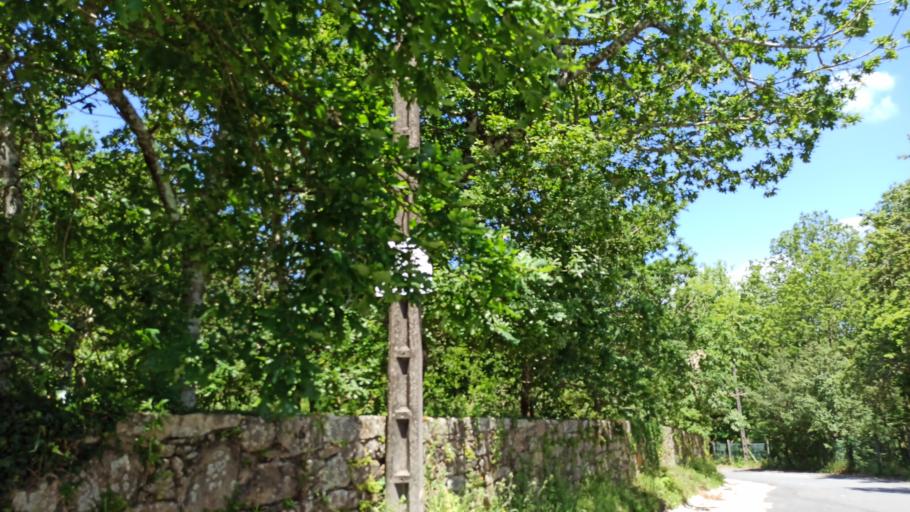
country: ES
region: Galicia
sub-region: Provincia da Coruna
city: Negreira
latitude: 42.9066
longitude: -8.7248
